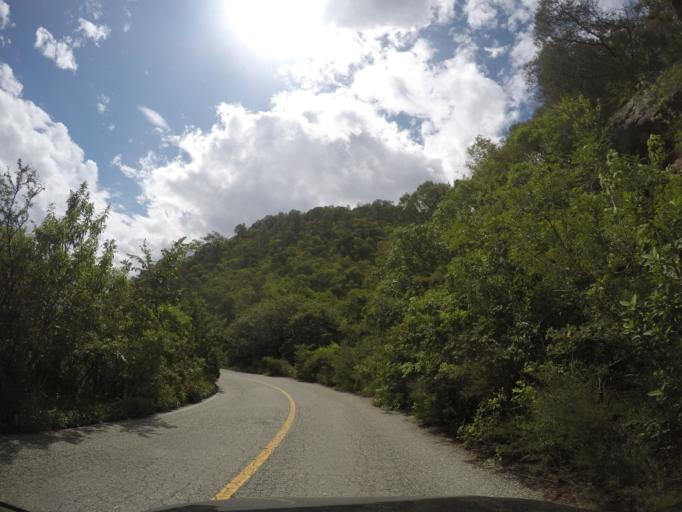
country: MX
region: Oaxaca
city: San Francisco Sola
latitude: 16.4324
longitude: -97.0393
